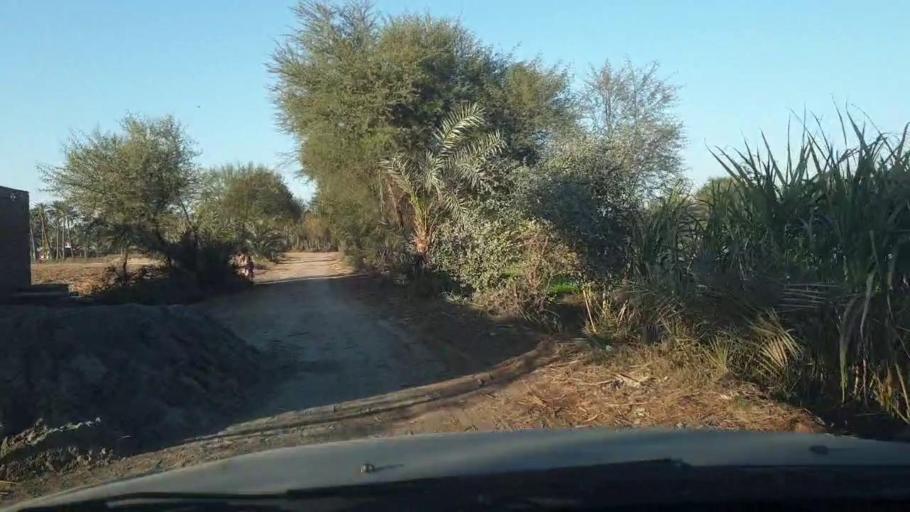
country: PK
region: Sindh
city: Ghotki
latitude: 28.0261
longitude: 69.3081
